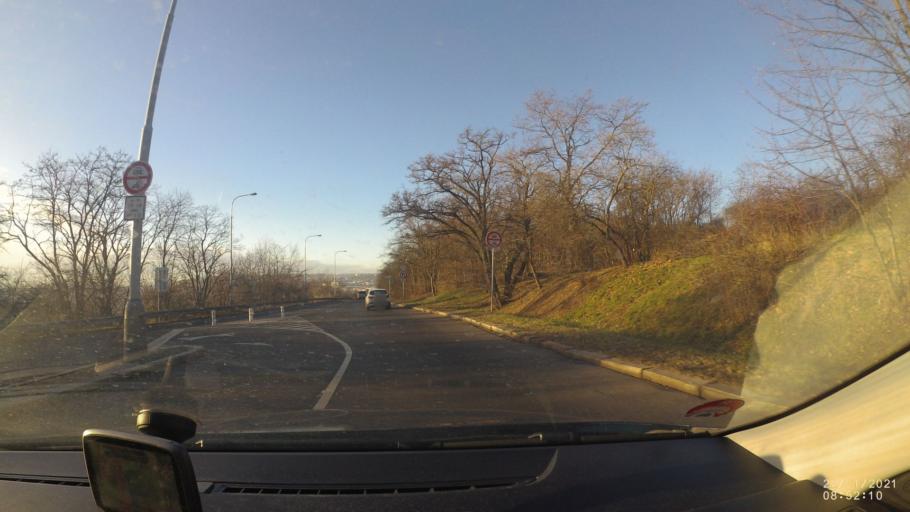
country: CZ
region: Praha
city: Prague
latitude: 50.1243
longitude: 14.4147
